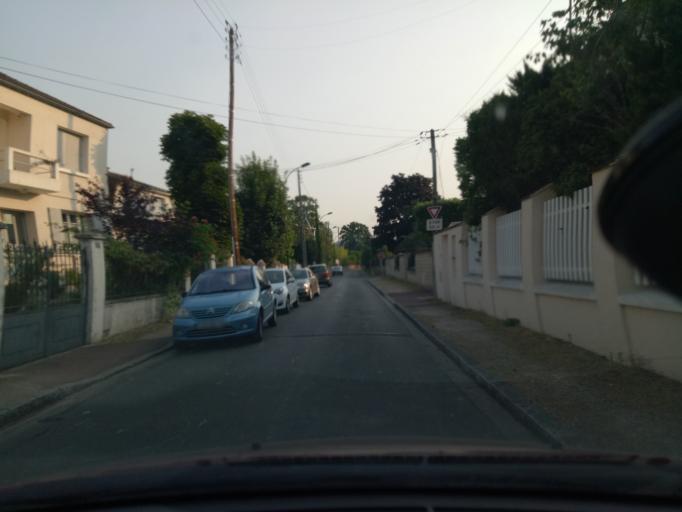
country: FR
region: Ile-de-France
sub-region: Departement des Yvelines
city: Croissy-sur-Seine
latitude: 48.8850
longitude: 2.1455
